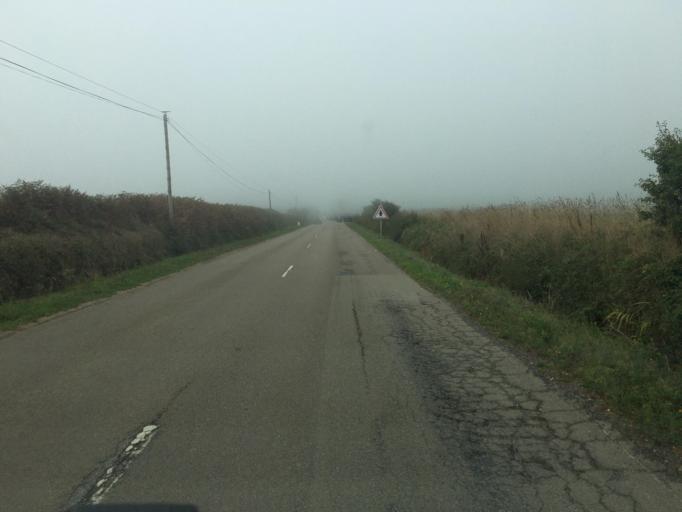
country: FR
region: Brittany
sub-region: Departement du Finistere
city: Plogoff
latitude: 48.0636
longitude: -4.6106
